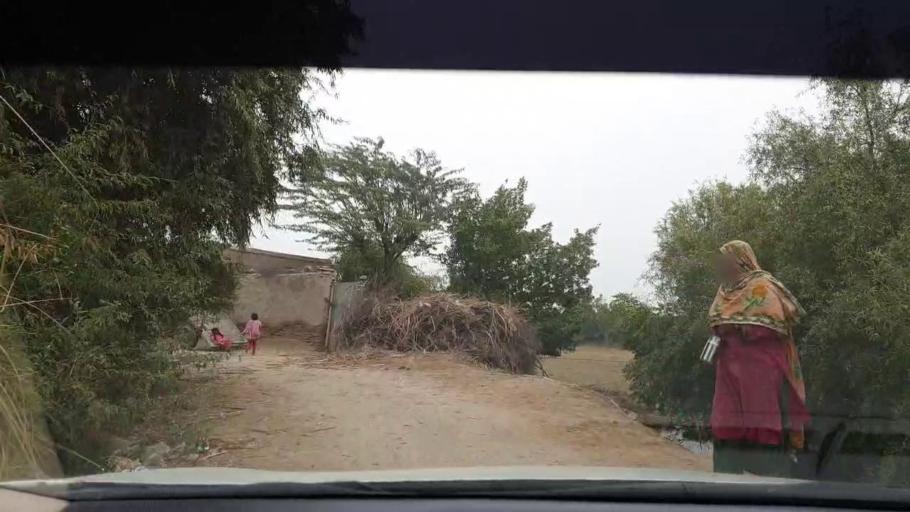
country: PK
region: Sindh
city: Berani
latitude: 25.8750
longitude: 68.7951
